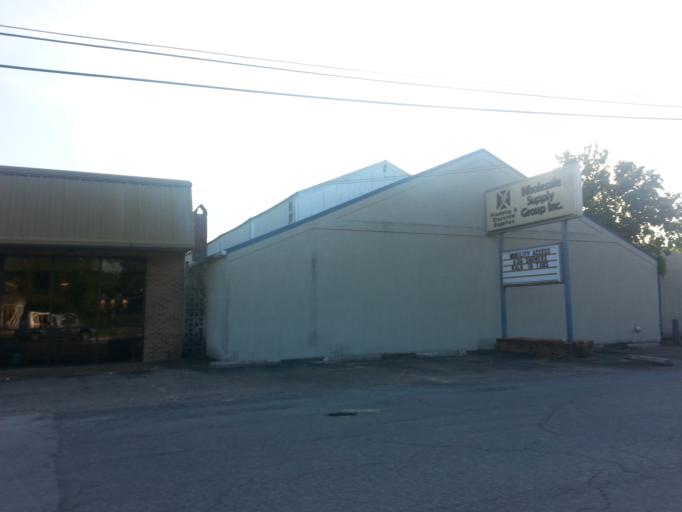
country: US
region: Tennessee
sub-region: McMinn County
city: Athens
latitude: 35.4538
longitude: -84.5999
